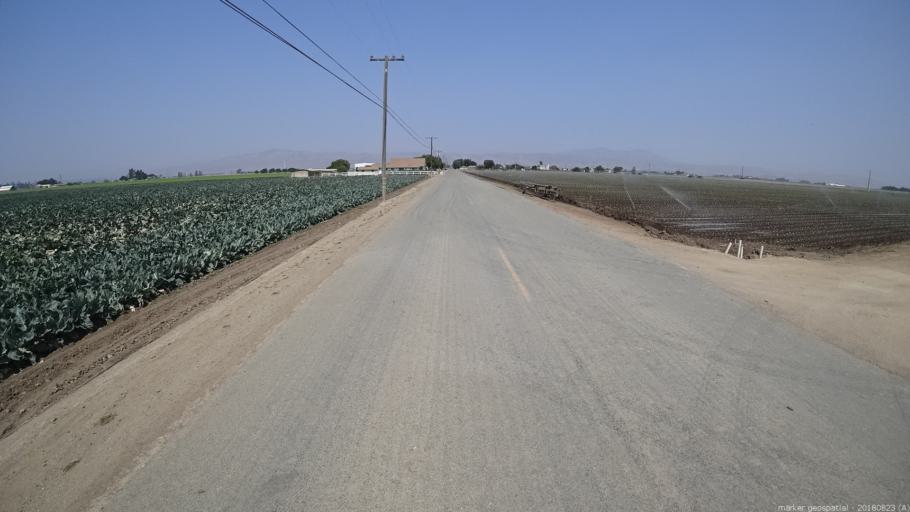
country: US
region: California
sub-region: Monterey County
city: Soledad
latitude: 36.3965
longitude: -121.3512
